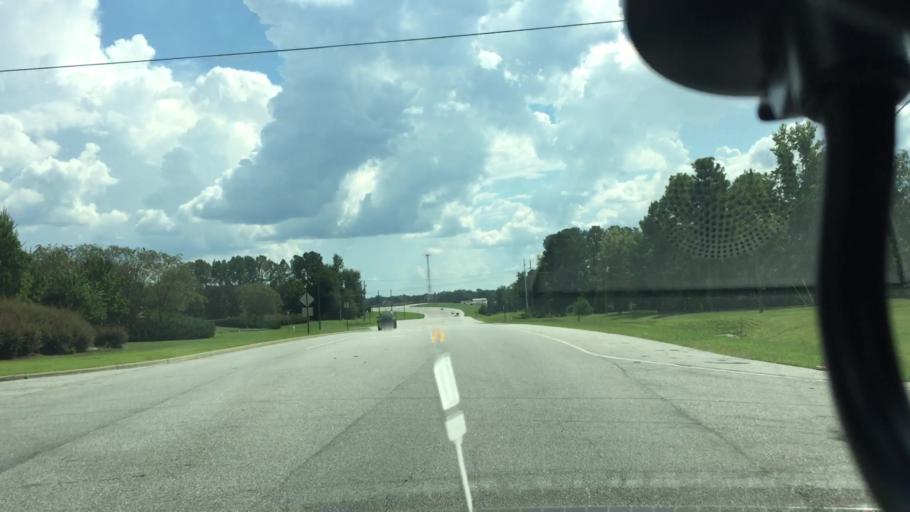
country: US
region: Alabama
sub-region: Lee County
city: Auburn
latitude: 32.5566
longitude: -85.5279
